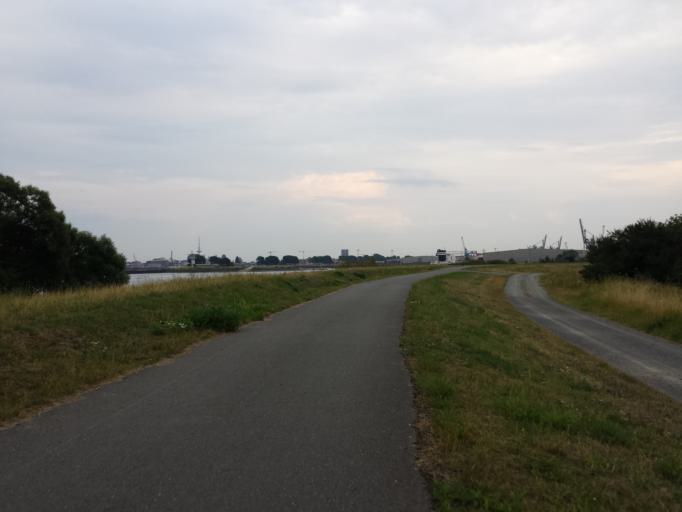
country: DE
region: Lower Saxony
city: Ritterhude
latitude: 53.1122
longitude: 8.7260
